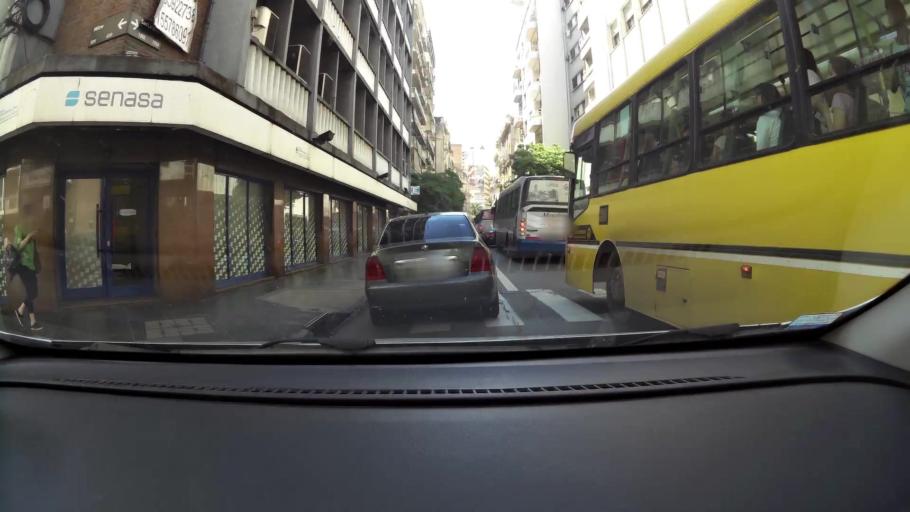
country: AR
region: Santa Fe
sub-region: Departamento de Rosario
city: Rosario
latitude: -32.9439
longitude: -60.6390
